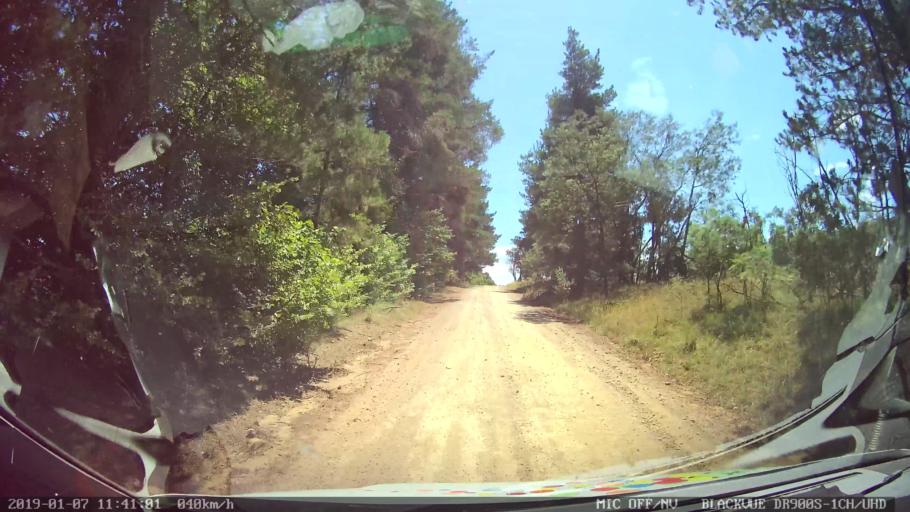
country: AU
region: New South Wales
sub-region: Armidale Dumaresq
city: Armidale
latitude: -30.3623
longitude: 151.5872
